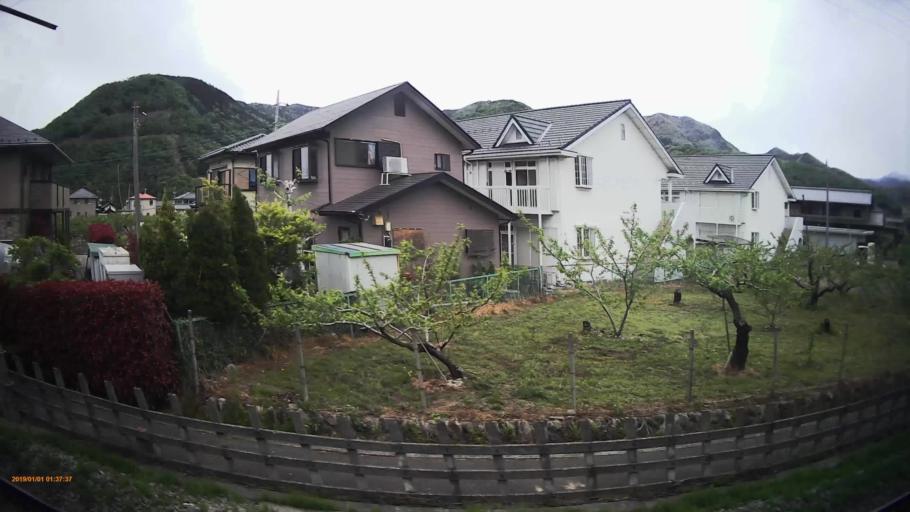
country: JP
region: Yamanashi
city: Isawa
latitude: 35.6644
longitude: 138.6475
